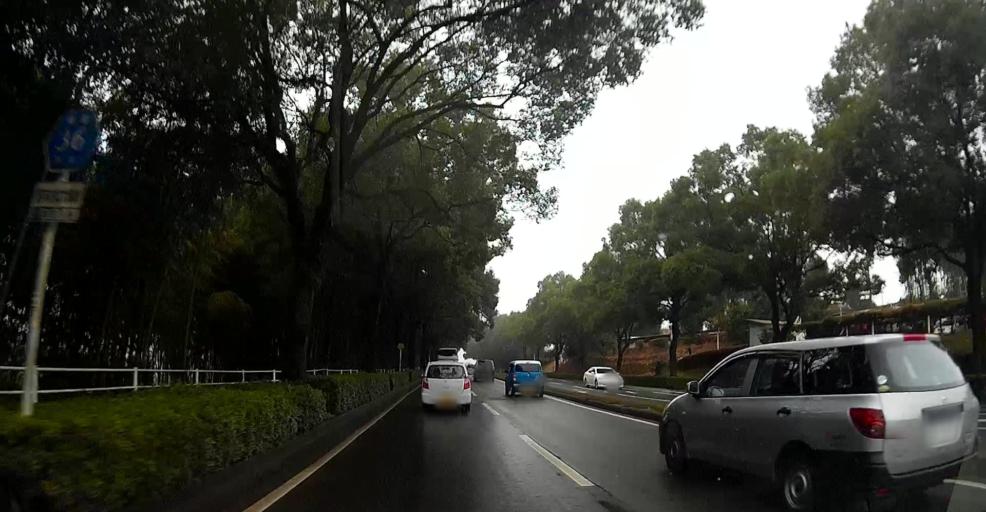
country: JP
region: Kumamoto
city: Ozu
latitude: 32.8239
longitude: 130.8561
